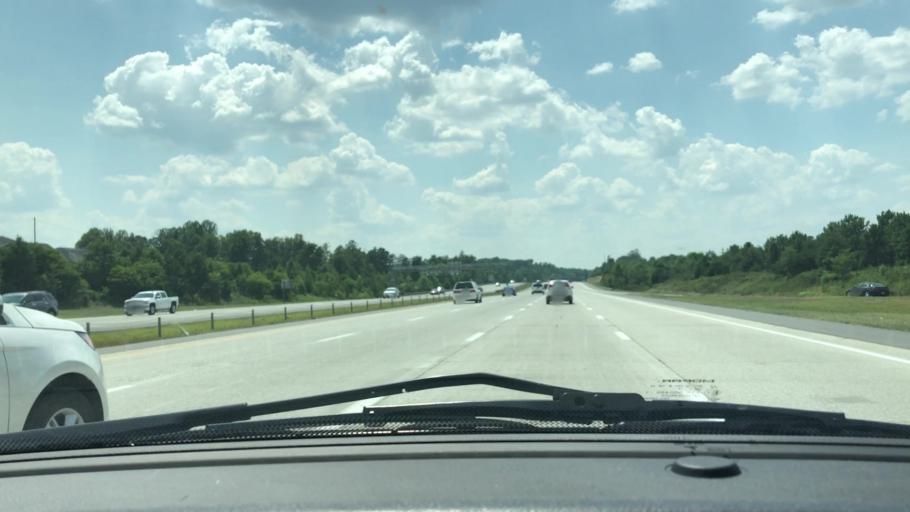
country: US
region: North Carolina
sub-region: Guilford County
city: Pleasant Garden
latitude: 36.0009
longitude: -79.7942
